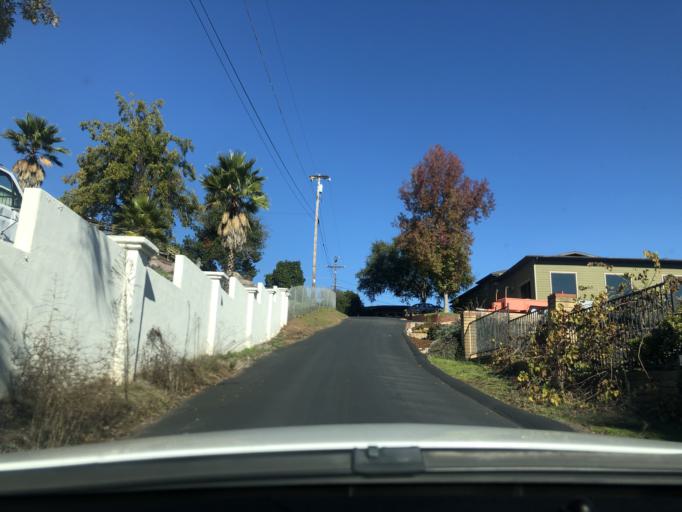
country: US
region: California
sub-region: San Diego County
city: Casa de Oro-Mount Helix
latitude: 32.7736
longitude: -116.9486
